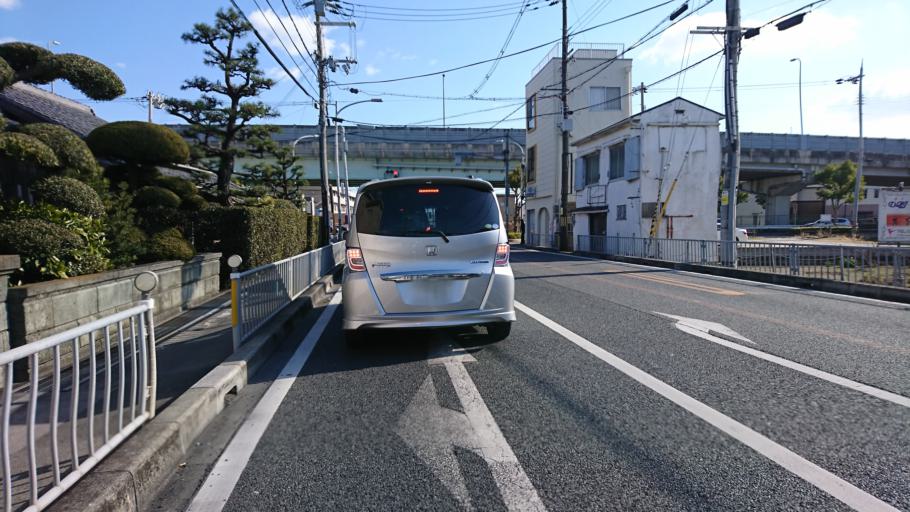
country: JP
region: Hyogo
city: Kakogawacho-honmachi
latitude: 34.7820
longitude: 134.8149
